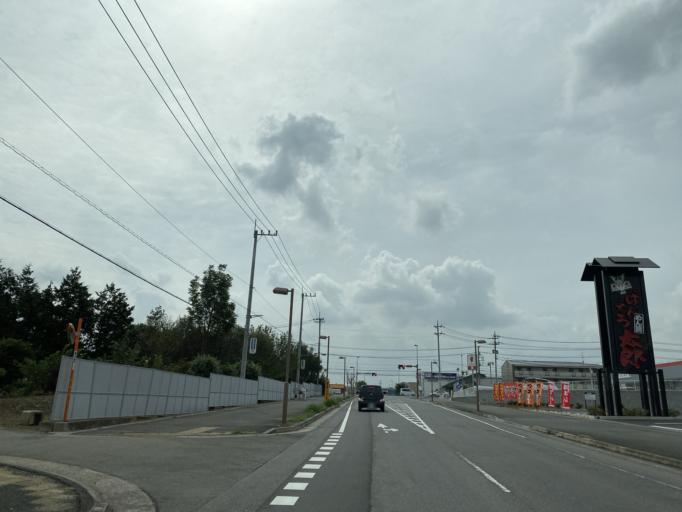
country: JP
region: Ibaraki
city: Mitsukaido
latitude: 36.0329
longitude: 140.0540
